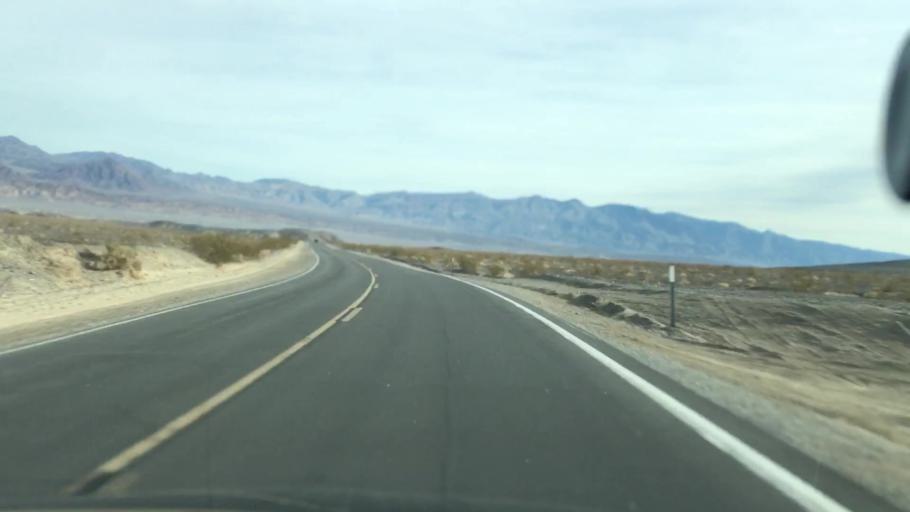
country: US
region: Nevada
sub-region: Nye County
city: Beatty
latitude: 36.6024
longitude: -117.0938
